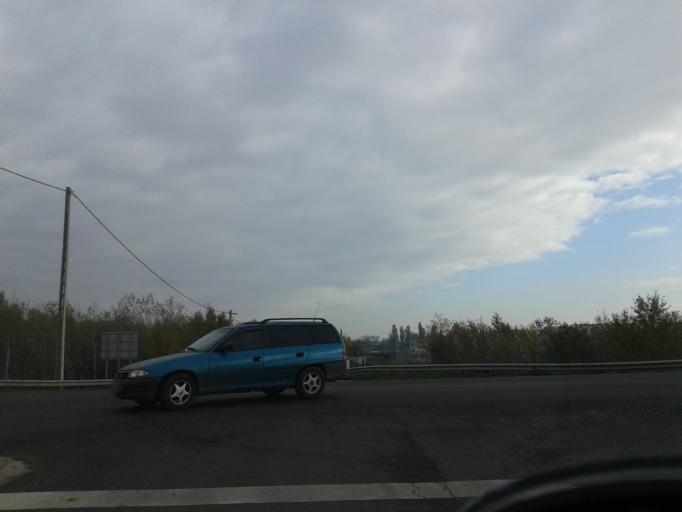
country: HU
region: Fejer
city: Adony
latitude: 47.1132
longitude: 18.8711
